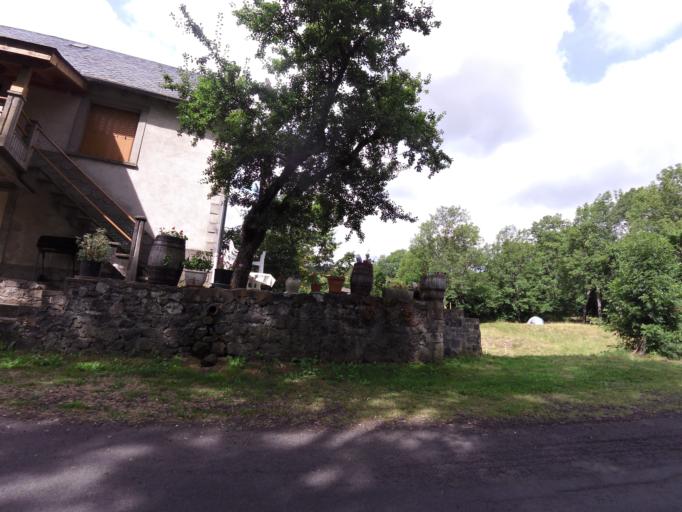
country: FR
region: Auvergne
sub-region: Departement du Puy-de-Dome
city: Mont-Dore
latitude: 45.4428
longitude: 2.9273
